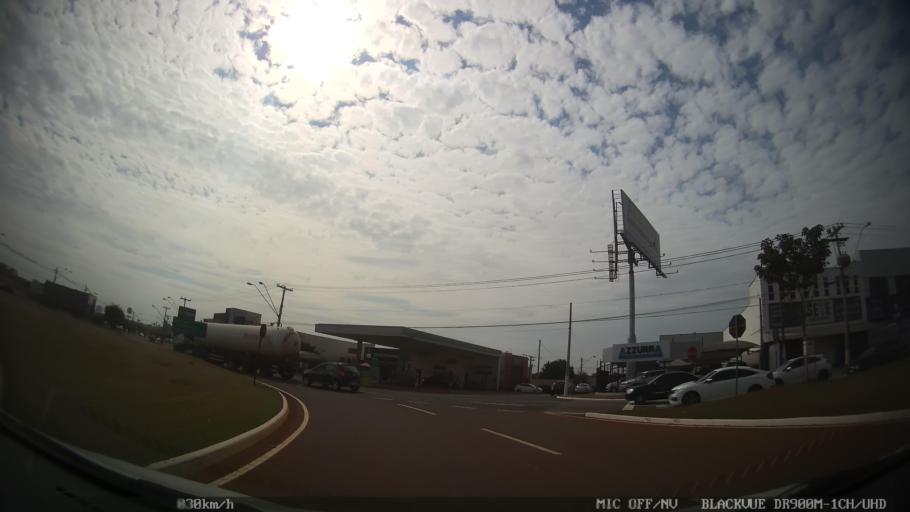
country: BR
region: Sao Paulo
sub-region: Paulinia
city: Paulinia
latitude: -22.7913
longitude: -47.1392
